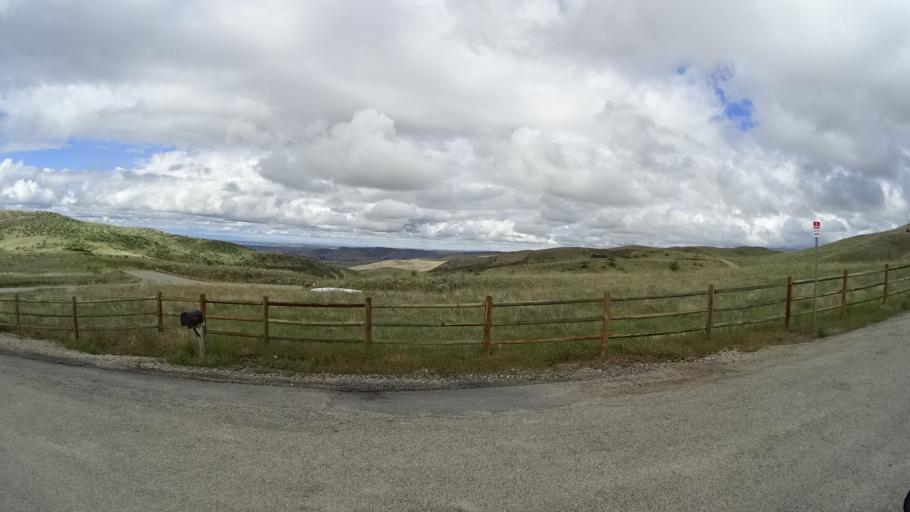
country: US
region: Idaho
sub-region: Ada County
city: Garden City
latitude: 43.7407
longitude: -116.2254
